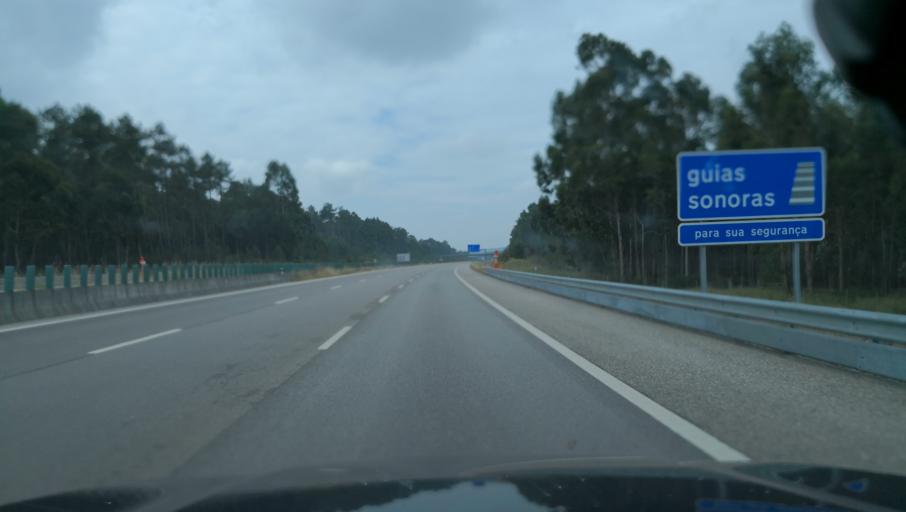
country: PT
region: Leiria
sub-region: Leiria
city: Monte Redondo
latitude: 39.8908
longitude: -8.8094
